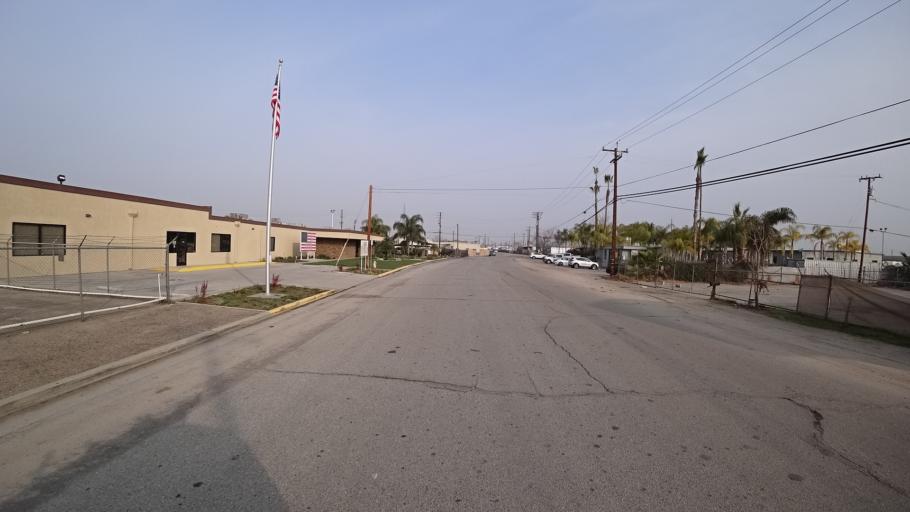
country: US
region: California
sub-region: Kern County
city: Bakersfield
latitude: 35.3875
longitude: -119.0477
